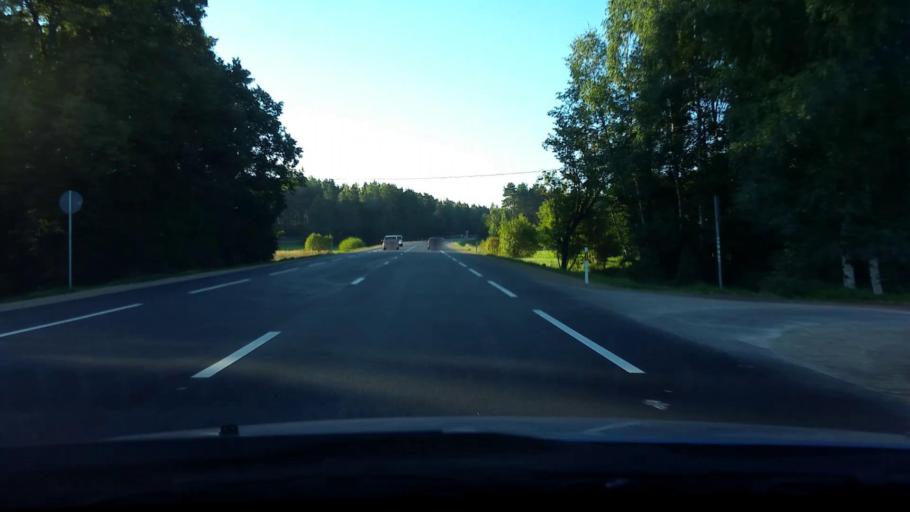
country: LV
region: Adazi
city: Adazi
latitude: 57.0636
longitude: 24.3214
